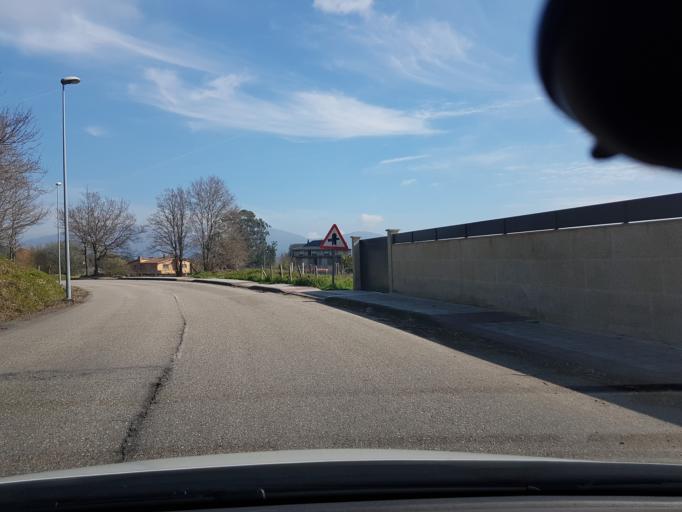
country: ES
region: Galicia
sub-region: Provincia de Pontevedra
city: Porrino
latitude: 42.1972
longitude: -8.6500
